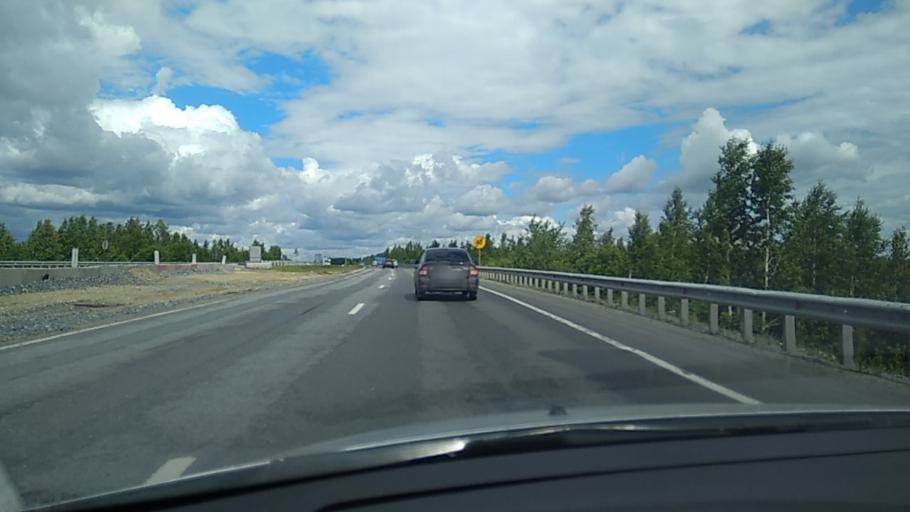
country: RU
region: Sverdlovsk
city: Nev'yansk
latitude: 57.4533
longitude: 60.1994
